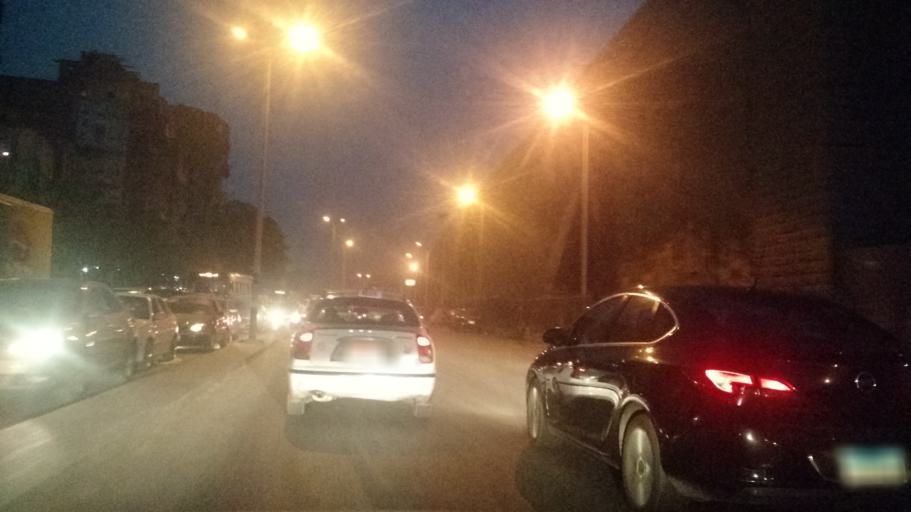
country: EG
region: Al Jizah
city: Al Jizah
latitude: 30.0218
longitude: 31.2344
